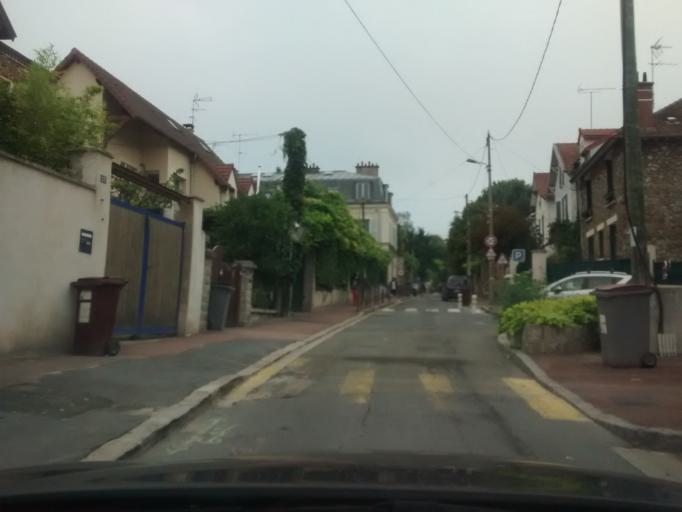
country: FR
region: Ile-de-France
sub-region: Departement des Yvelines
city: Viroflay
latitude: 48.8061
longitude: 2.1687
